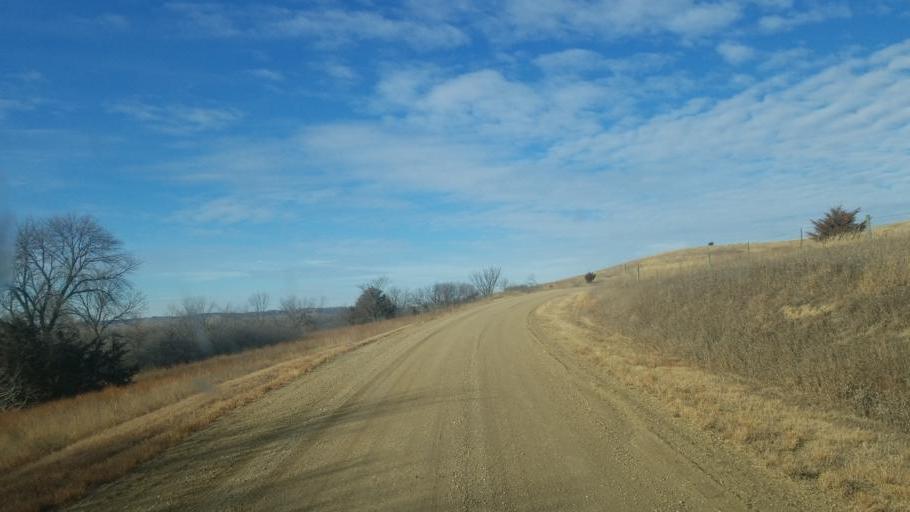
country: US
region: South Dakota
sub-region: Charles Mix County
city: Wagner
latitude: 42.9315
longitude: -98.4109
